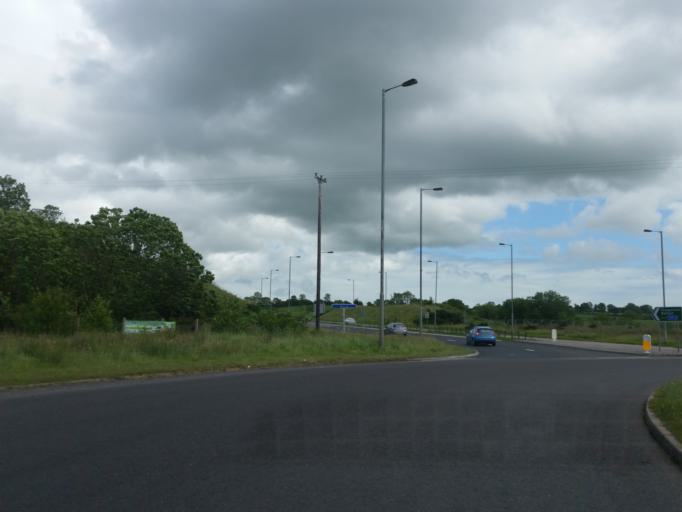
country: IE
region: Ulster
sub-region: County Monaghan
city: Monaghan
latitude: 54.4554
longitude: -7.0319
